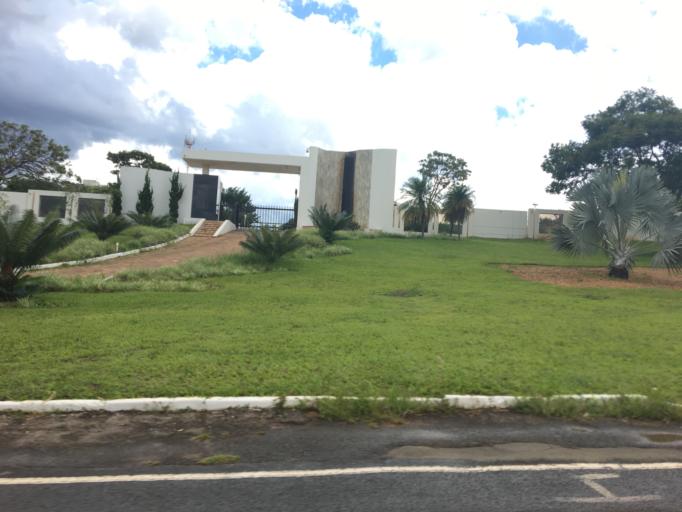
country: BR
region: Federal District
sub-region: Brasilia
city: Brasilia
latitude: -15.8962
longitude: -47.9128
